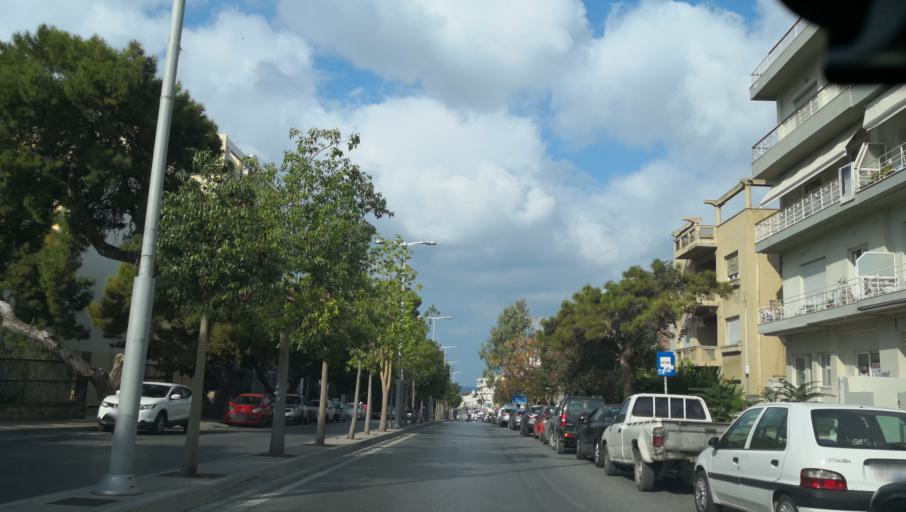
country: GR
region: Crete
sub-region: Nomos Irakleiou
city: Irakleion
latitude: 35.3335
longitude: 25.1386
